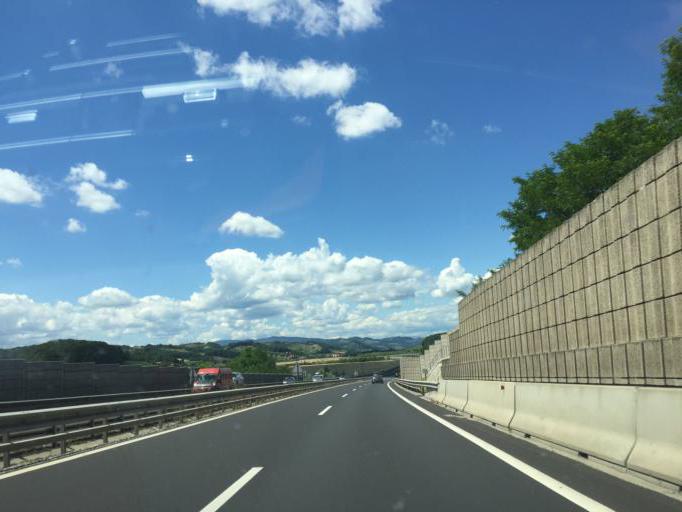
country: SI
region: Sveti Jurij v Slovenskih Goricah
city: Jurovski Dol
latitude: 46.5716
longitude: 15.7623
